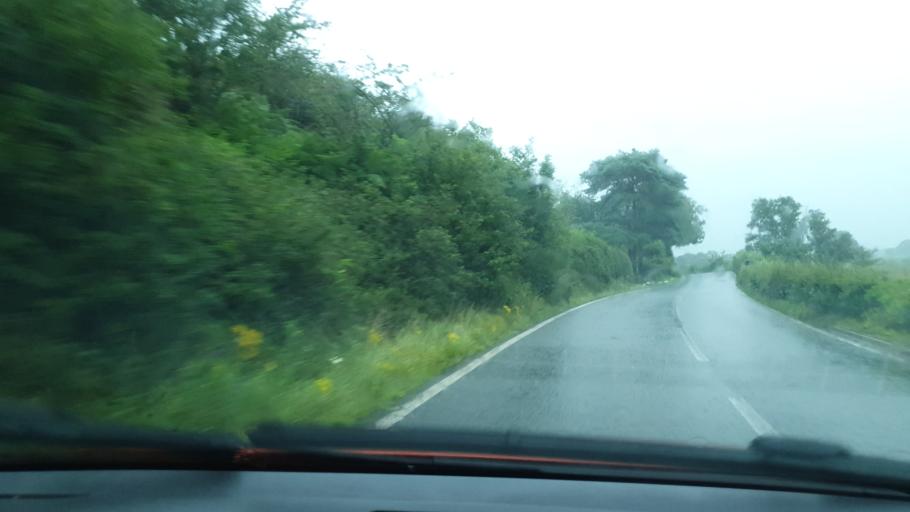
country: GB
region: England
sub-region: Cumbria
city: Askam in Furness
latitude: 54.2629
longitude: -3.2022
